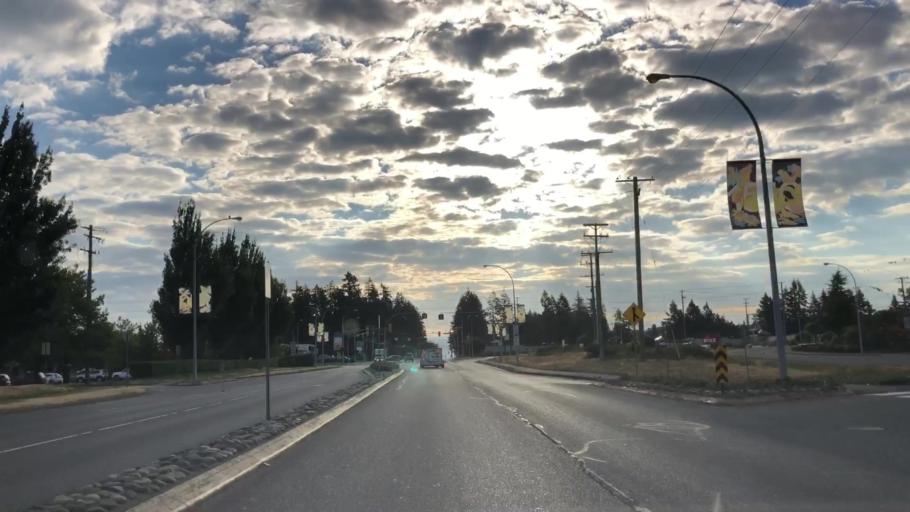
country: CA
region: British Columbia
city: Nanaimo
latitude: 49.2344
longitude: -124.0472
